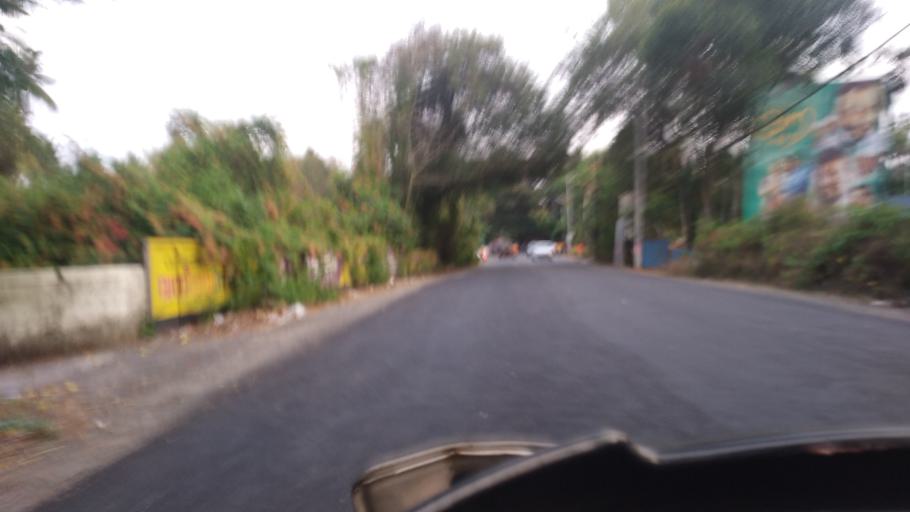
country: IN
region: Kerala
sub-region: Thrissur District
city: Kodungallur
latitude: 10.2474
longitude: 76.1889
